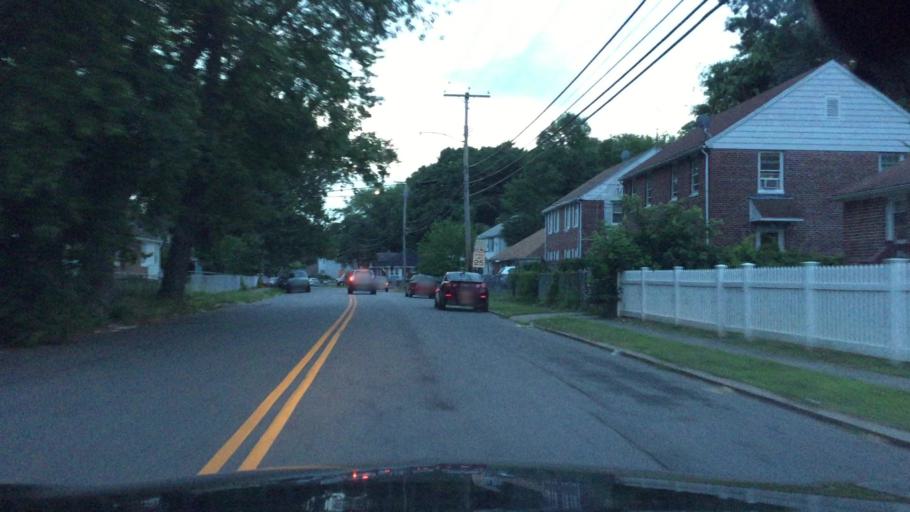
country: US
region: Connecticut
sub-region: Fairfield County
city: Stratford
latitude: 41.2022
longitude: -73.1609
